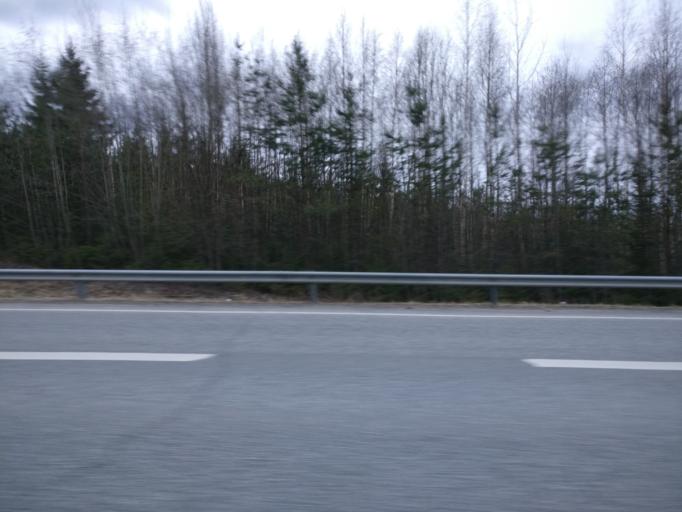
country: FI
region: Haeme
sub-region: Haemeenlinna
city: Tervakoski
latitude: 60.8192
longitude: 24.6710
